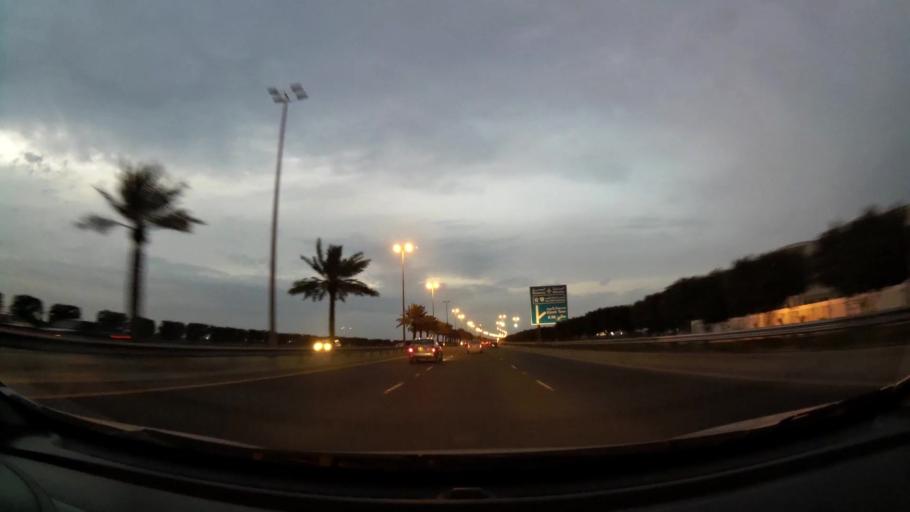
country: BH
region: Central Governorate
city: Madinat Hamad
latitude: 26.1572
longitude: 50.5060
